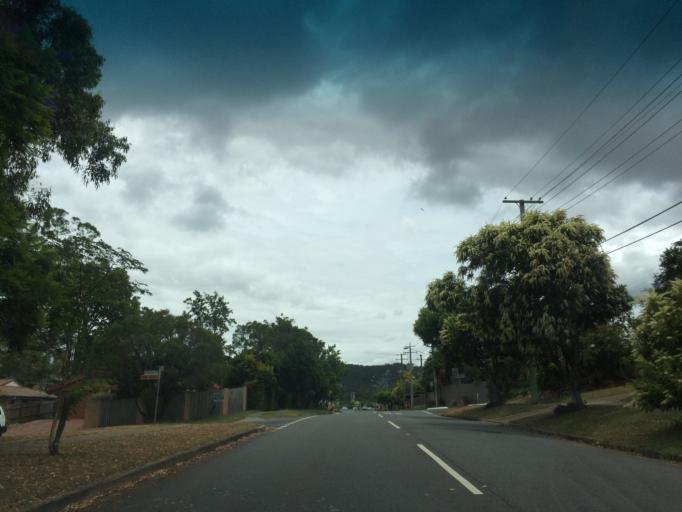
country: AU
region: Queensland
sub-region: Brisbane
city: Kenmore Hills
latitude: -27.5106
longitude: 152.9474
